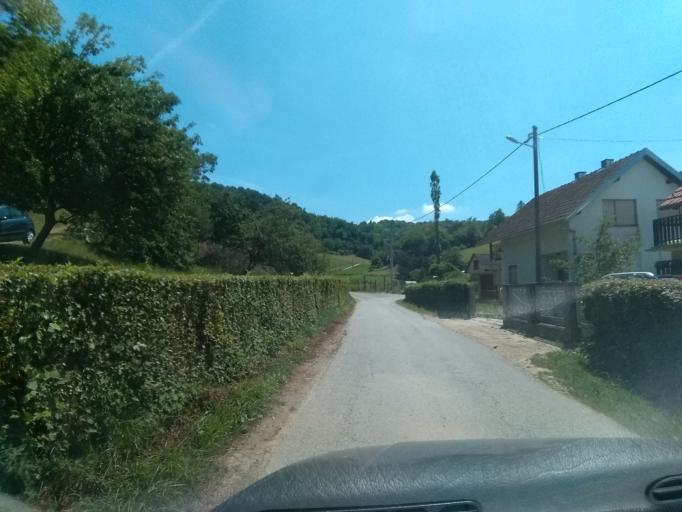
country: SI
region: Bistrica ob Sotli
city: Bistrica ob Sotli
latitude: 46.0733
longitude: 15.7441
